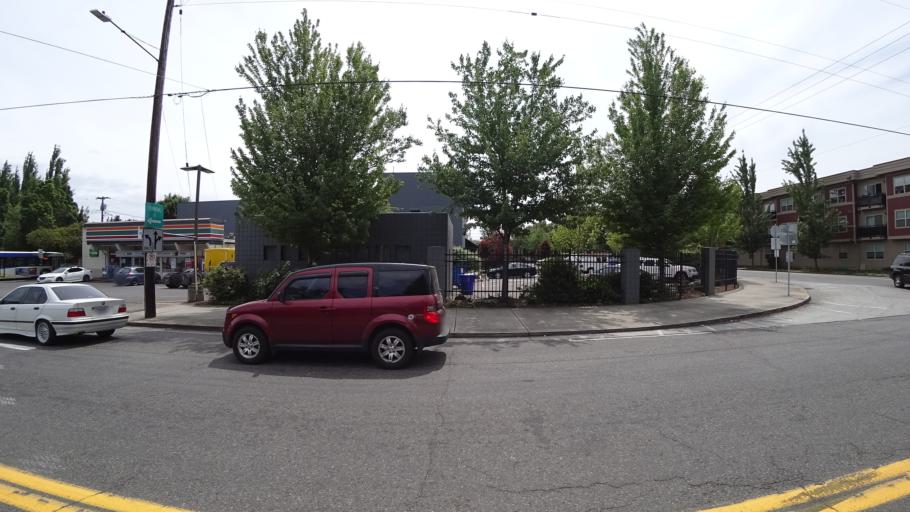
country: US
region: Oregon
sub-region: Washington County
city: West Haven
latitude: 45.5927
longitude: -122.7581
